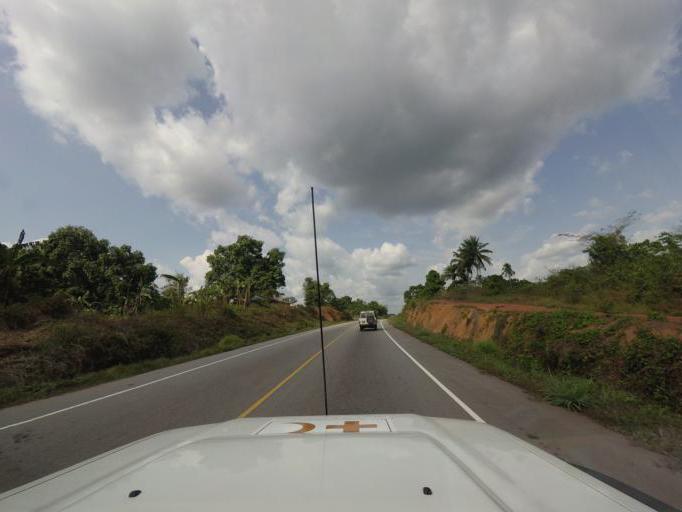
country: LR
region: Bong
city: Gbarnga
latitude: 6.8602
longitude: -9.7783
